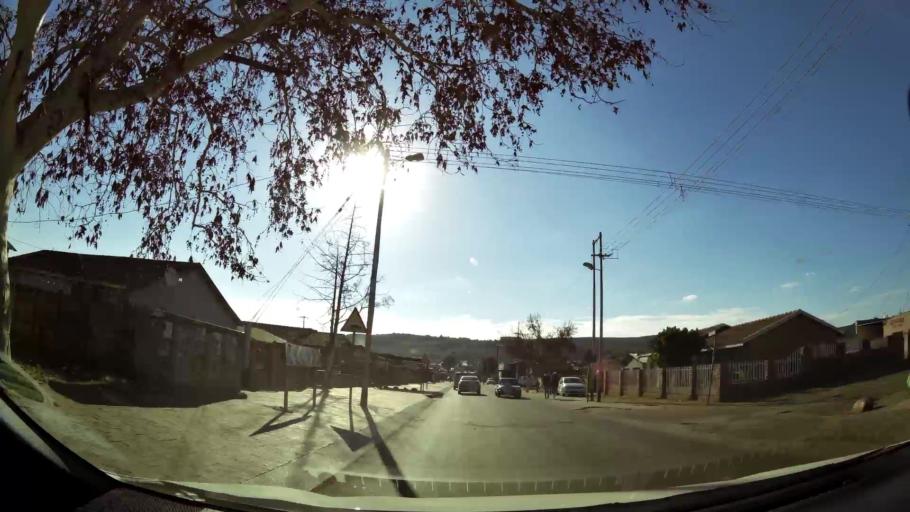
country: ZA
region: Gauteng
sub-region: City of Tshwane Metropolitan Municipality
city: Cullinan
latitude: -25.7090
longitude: 28.3890
